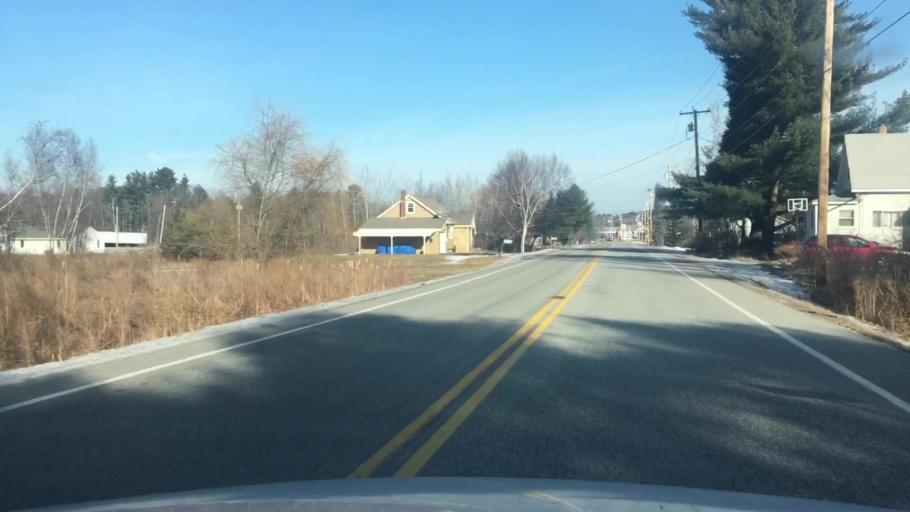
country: US
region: Maine
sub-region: Androscoggin County
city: Auburn
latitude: 44.0768
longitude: -70.2633
